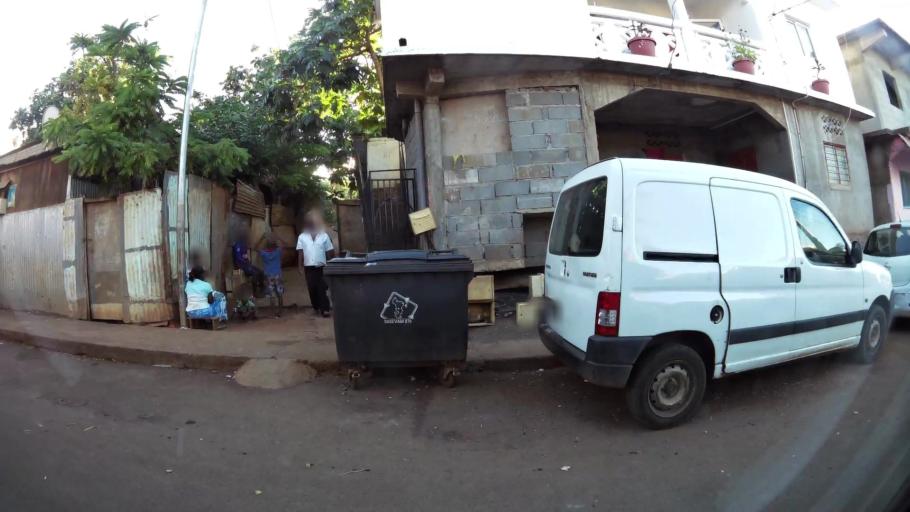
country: YT
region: Koungou
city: Koungou
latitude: -12.7344
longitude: 45.2052
